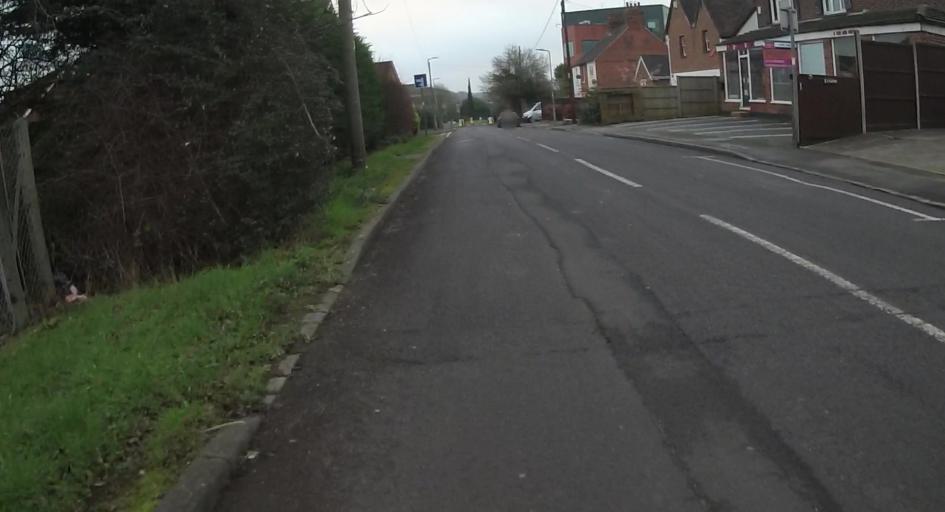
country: GB
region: England
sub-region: Bracknell Forest
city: Binfield
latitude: 51.4168
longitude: -0.7853
